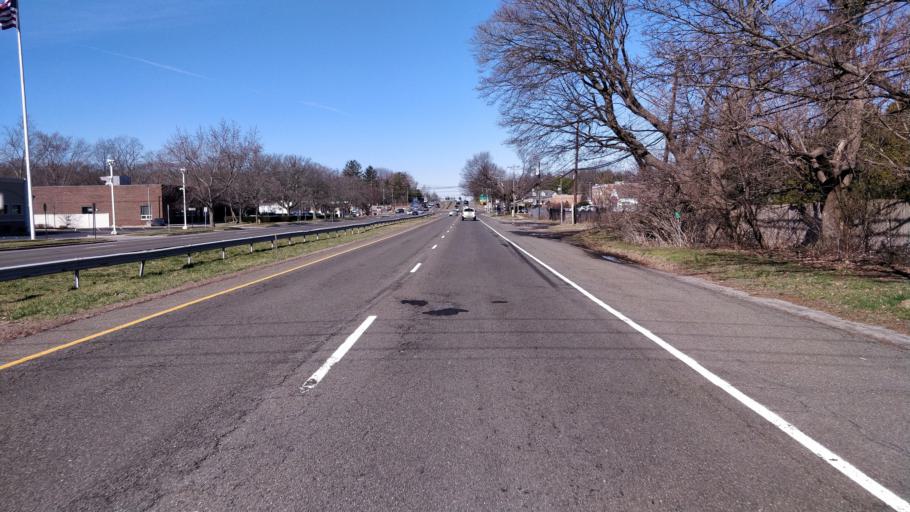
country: US
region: New York
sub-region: Suffolk County
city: Commack
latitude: 40.8380
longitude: -73.2760
